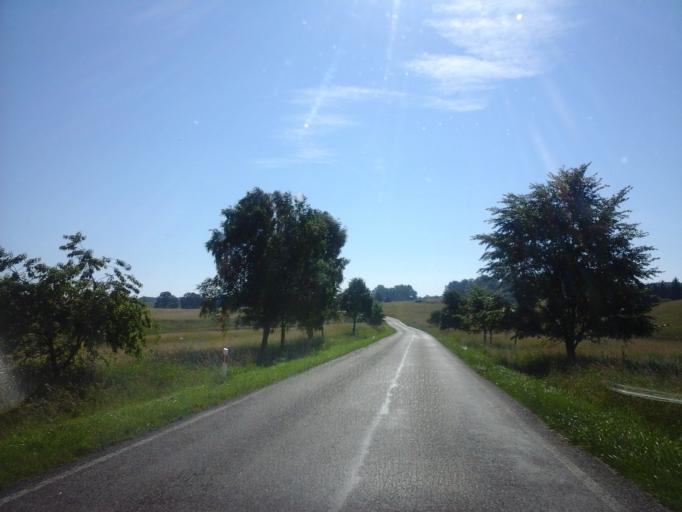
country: PL
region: West Pomeranian Voivodeship
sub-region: Powiat drawski
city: Zlocieniec
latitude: 53.6398
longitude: 15.9915
